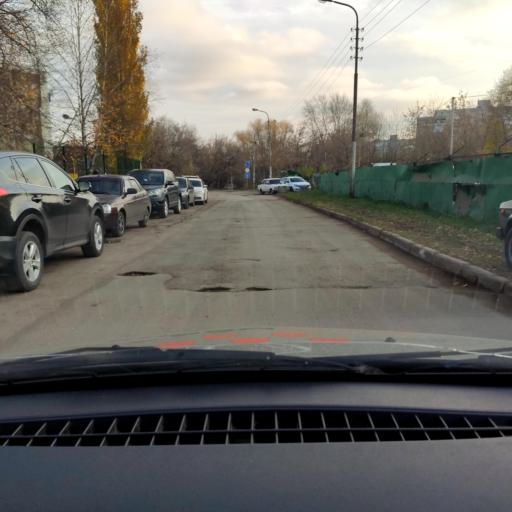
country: RU
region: Bashkortostan
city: Ufa
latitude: 54.7432
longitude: 55.9999
